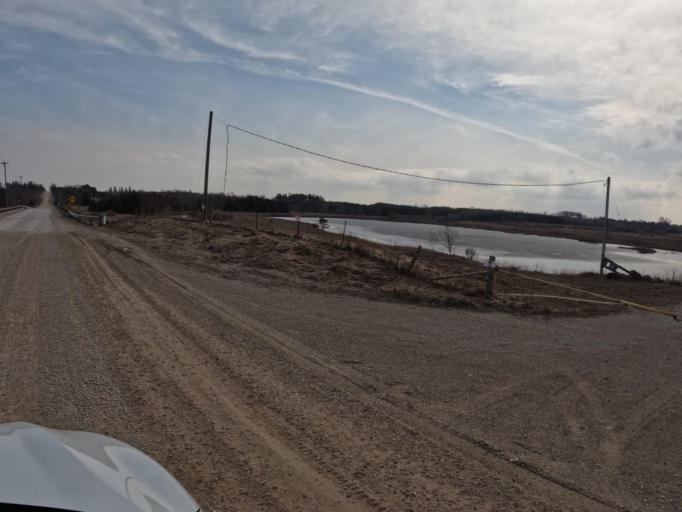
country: CA
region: Ontario
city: Orangeville
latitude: 43.8947
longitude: -80.3001
